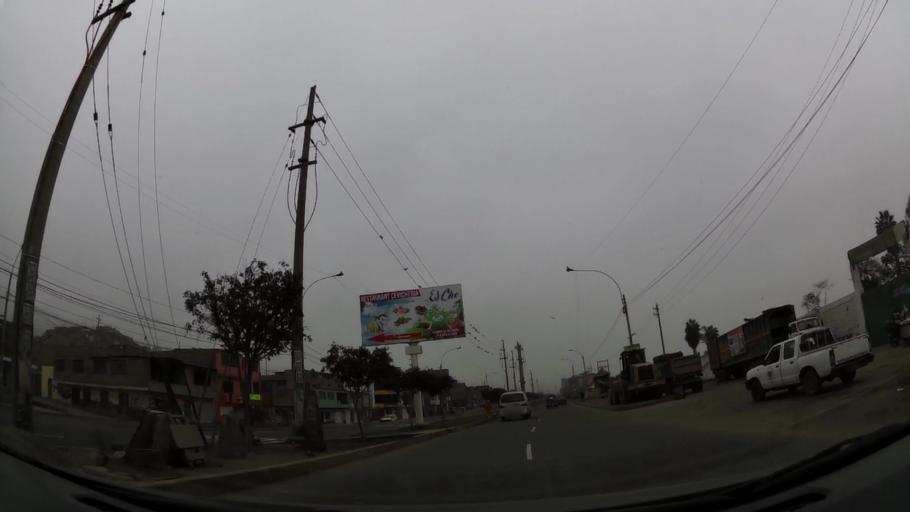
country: PE
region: Lima
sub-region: Lima
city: Urb. Santo Domingo
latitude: -11.8876
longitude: -77.0240
